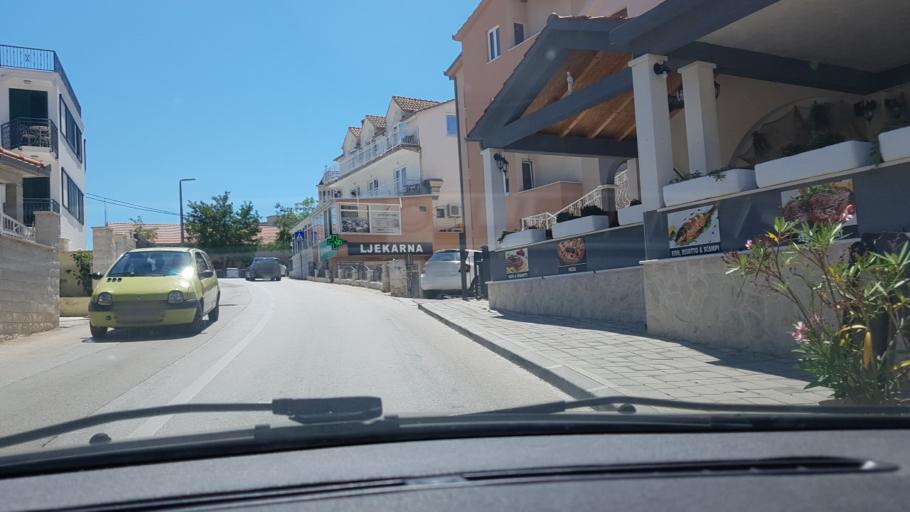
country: HR
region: Splitsko-Dalmatinska
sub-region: Grad Trogir
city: Trogir
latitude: 43.4941
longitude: 16.2637
